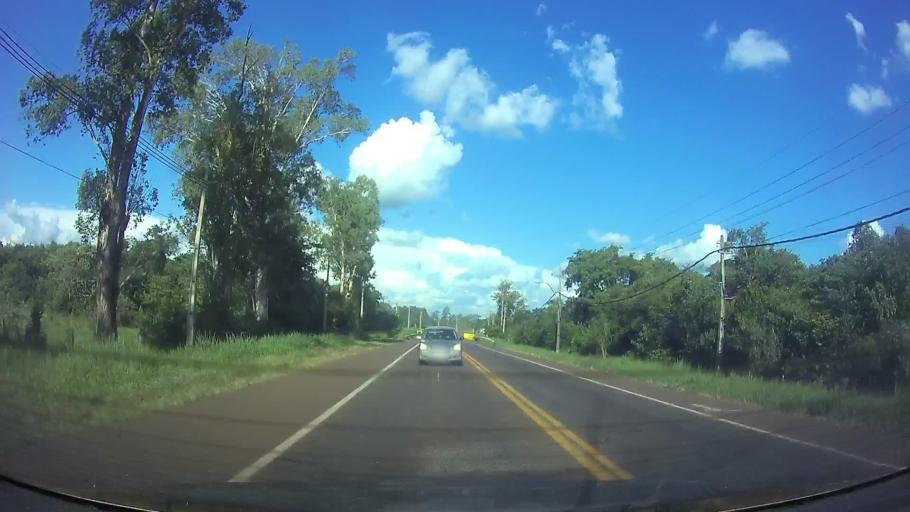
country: PY
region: Cordillera
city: Eusebio Ayala
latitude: -25.3805
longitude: -56.9899
